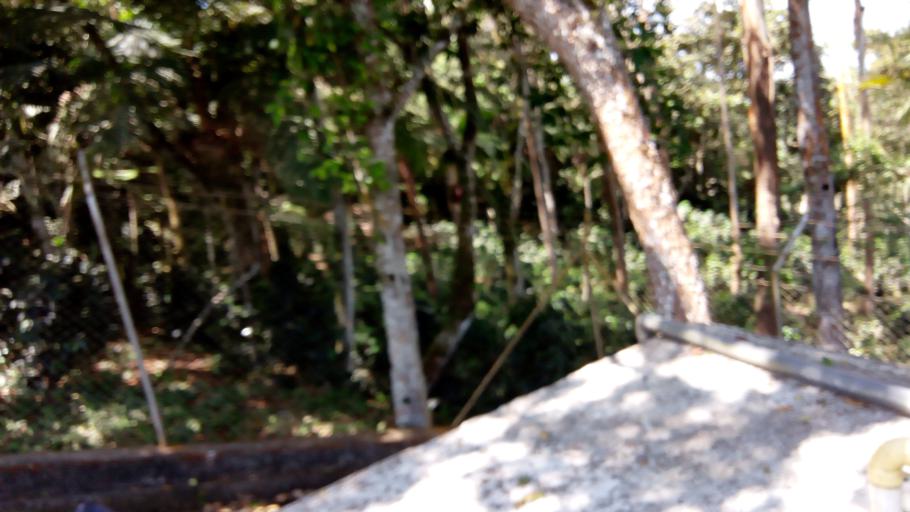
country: CO
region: Valle del Cauca
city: Cali
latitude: 3.5024
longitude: -76.5861
